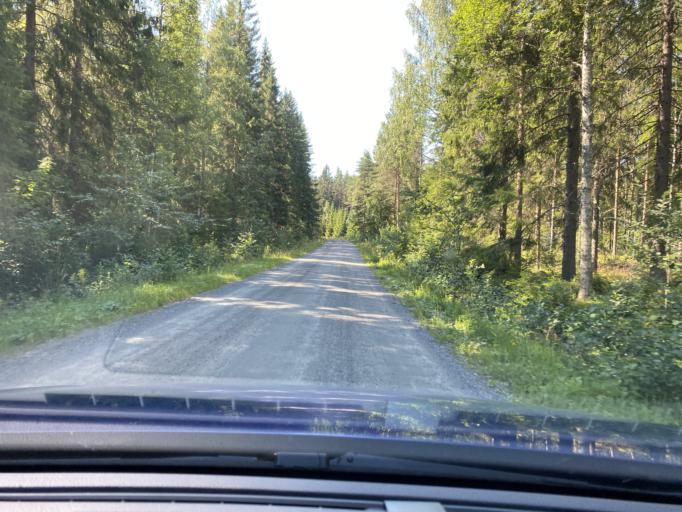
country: FI
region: Central Finland
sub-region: Jyvaeskylae
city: Korpilahti
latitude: 61.8695
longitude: 25.4015
